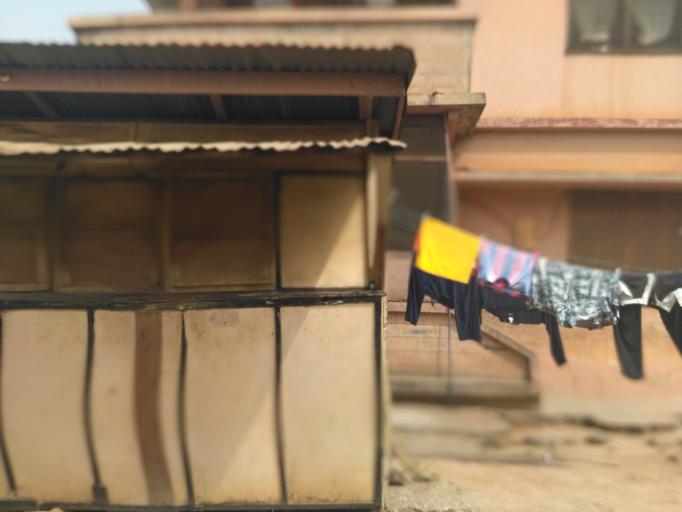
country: GH
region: Ashanti
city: Kumasi
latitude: 6.6835
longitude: -1.6022
